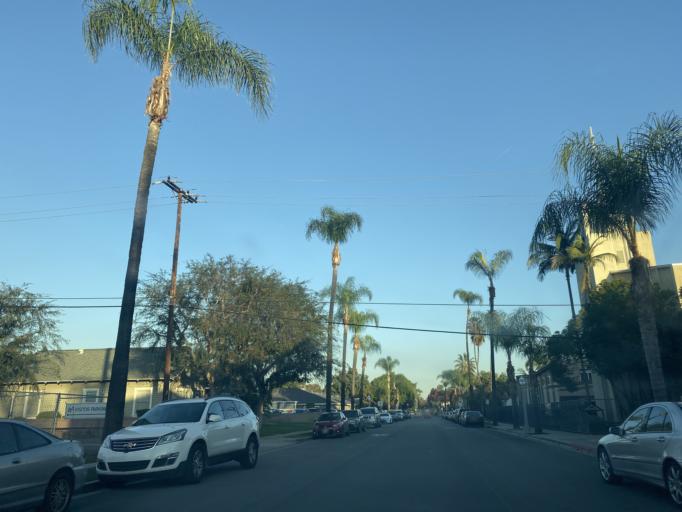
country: US
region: California
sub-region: Orange County
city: Fullerton
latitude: 33.8724
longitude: -117.9218
